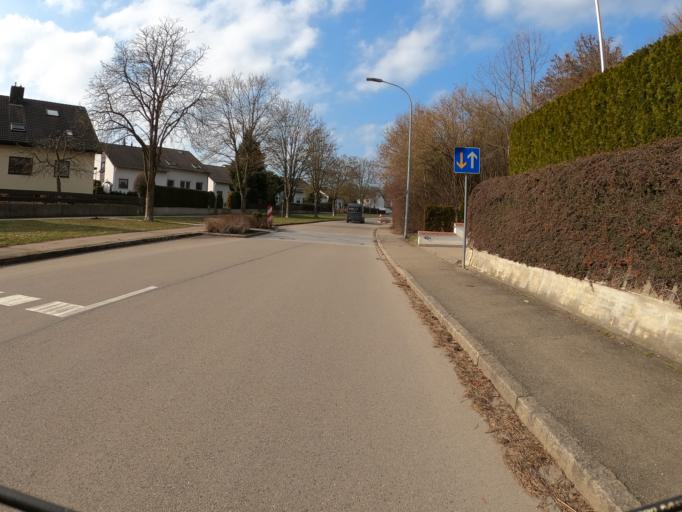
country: DE
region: Baden-Wuerttemberg
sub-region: Tuebingen Region
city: Bernstadt
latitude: 48.4439
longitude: 10.0491
